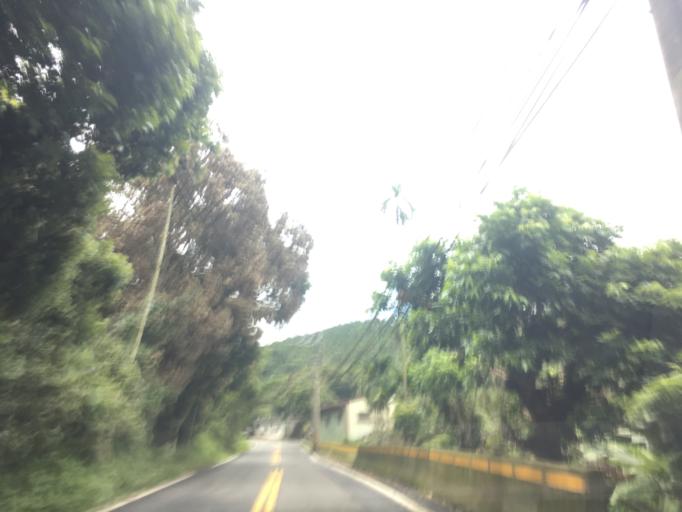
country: TW
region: Taiwan
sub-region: Yunlin
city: Douliu
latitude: 23.5655
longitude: 120.5744
